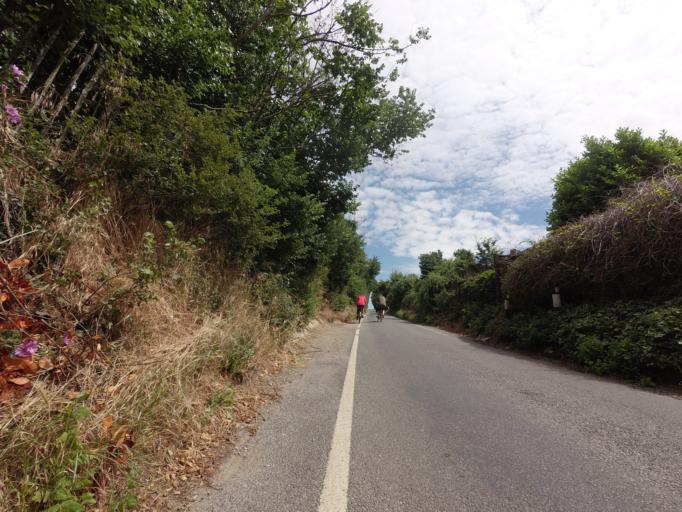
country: GB
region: England
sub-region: Kent
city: Strood
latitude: 51.4289
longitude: 0.4668
